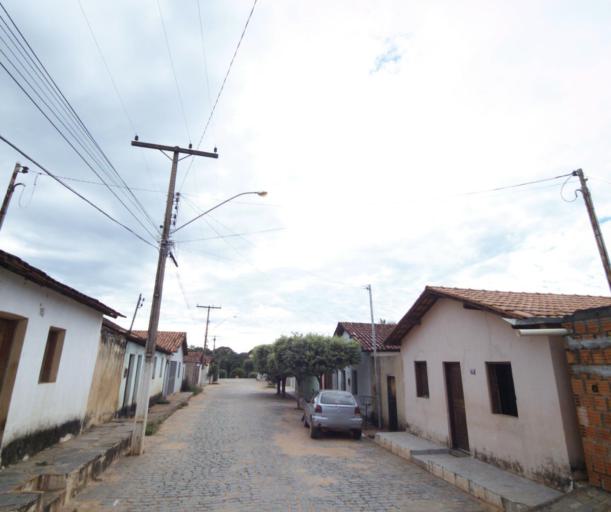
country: BR
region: Bahia
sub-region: Carinhanha
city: Carinhanha
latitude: -14.1785
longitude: -44.5307
